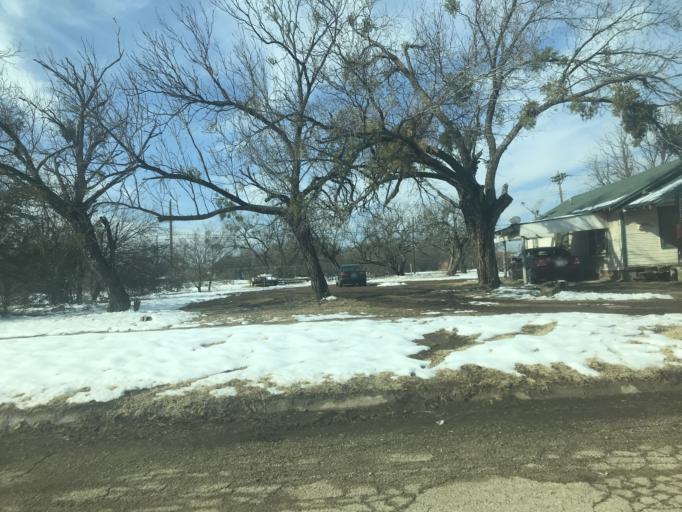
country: US
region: Texas
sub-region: Taylor County
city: Abilene
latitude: 32.4616
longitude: -99.7279
